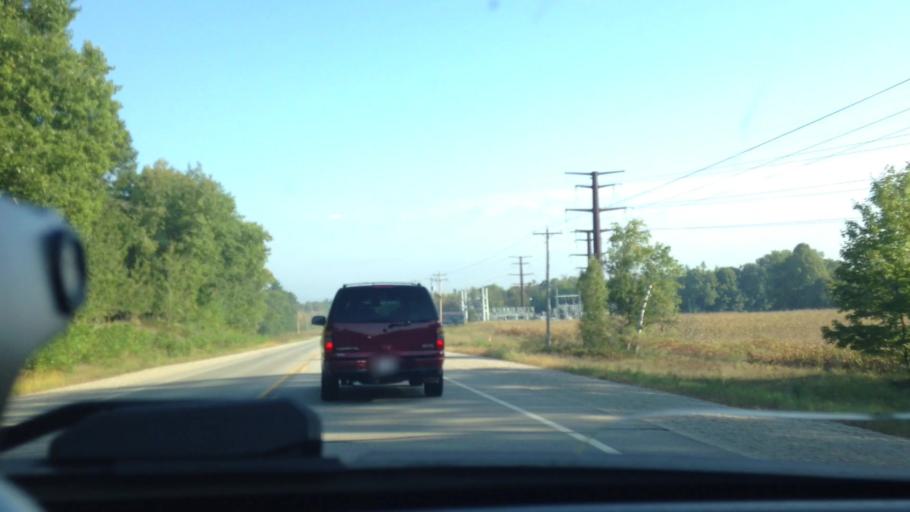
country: US
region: Wisconsin
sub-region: Marinette County
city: Peshtigo
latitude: 45.1739
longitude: -87.9960
